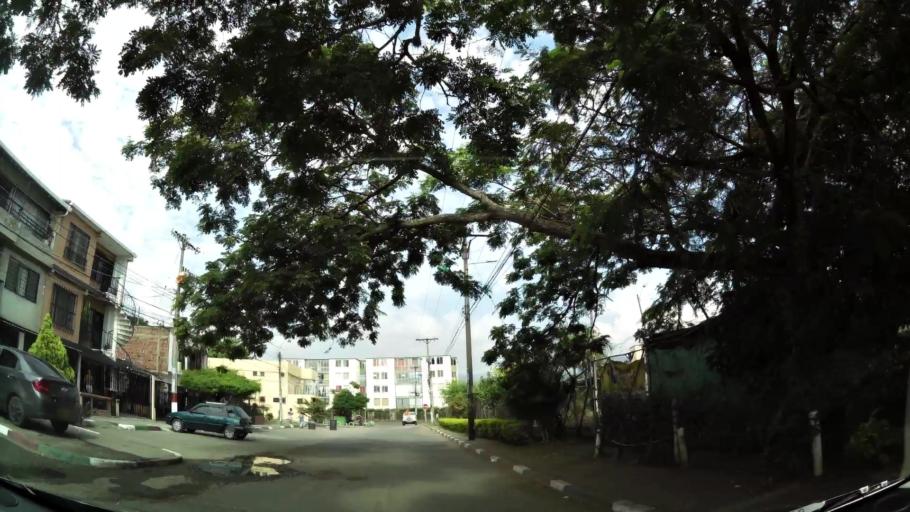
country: CO
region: Valle del Cauca
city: Cali
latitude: 3.4910
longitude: -76.4962
